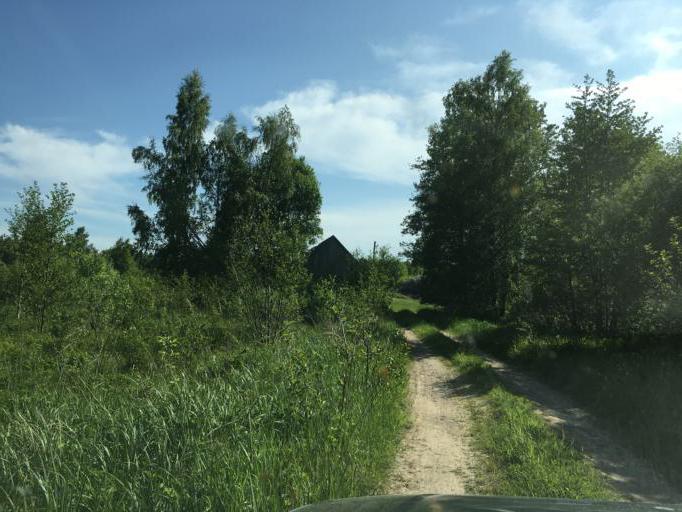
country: LV
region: Dundaga
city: Dundaga
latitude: 57.6008
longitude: 22.5072
